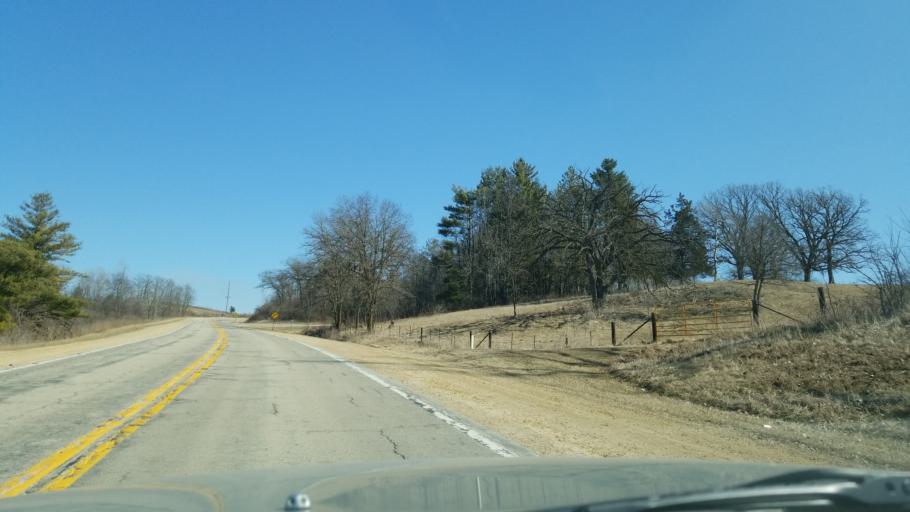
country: US
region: Wisconsin
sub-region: Iowa County
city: Mineral Point
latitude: 42.9131
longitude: -90.2638
